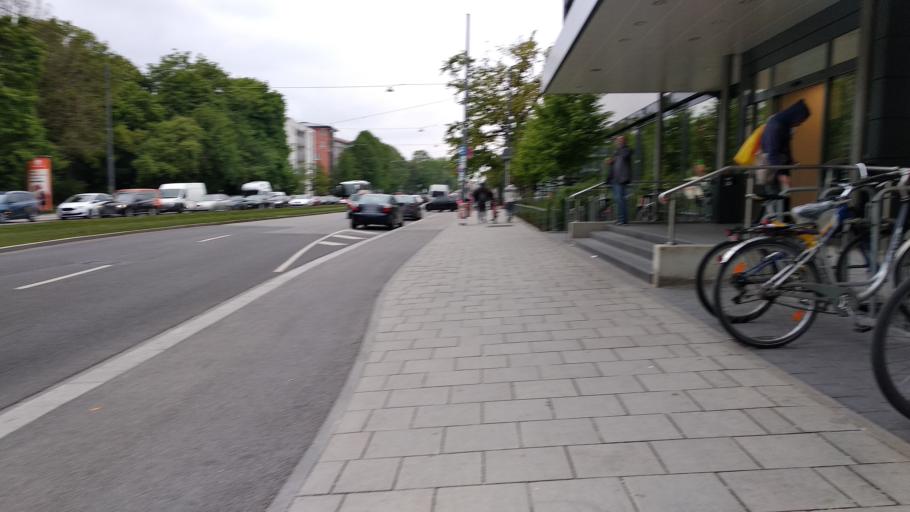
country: DE
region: Bavaria
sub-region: Upper Bavaria
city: Bogenhausen
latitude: 48.1294
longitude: 11.6265
